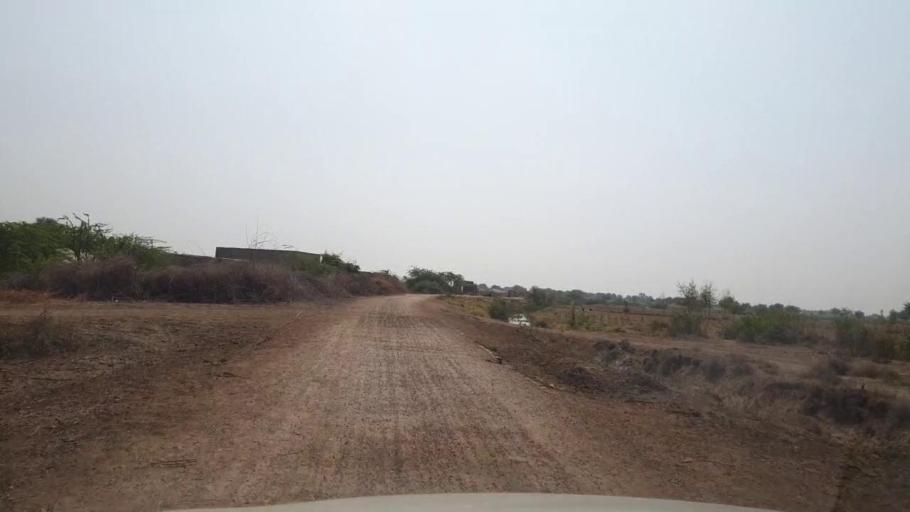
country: PK
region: Sindh
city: Dhoro Naro
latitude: 25.4883
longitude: 69.6451
